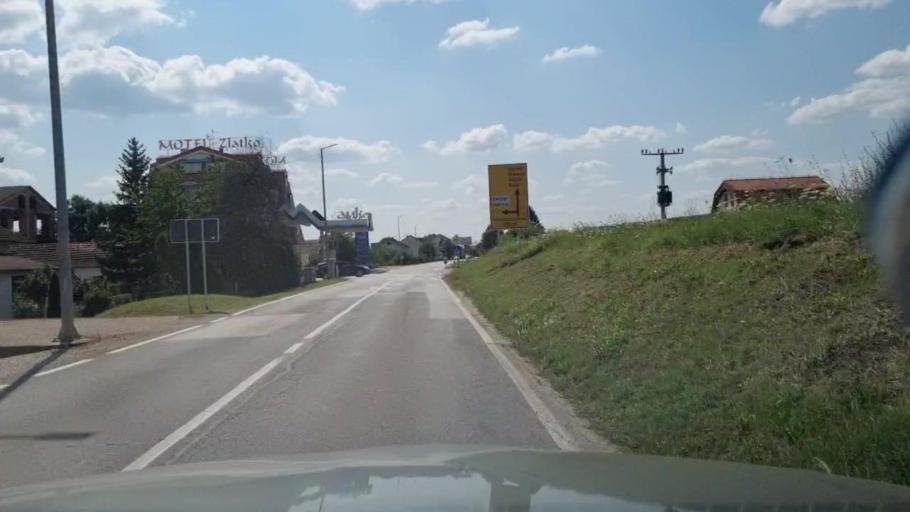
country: HR
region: Vukovarsko-Srijemska
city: Stitar
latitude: 45.0633
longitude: 18.5878
